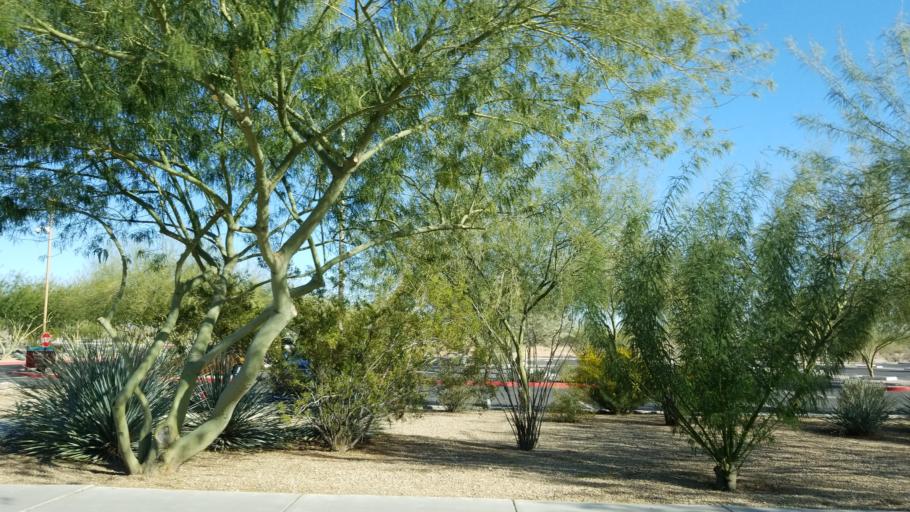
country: US
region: Arizona
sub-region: Maricopa County
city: Paradise Valley
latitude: 33.6565
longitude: -111.9562
